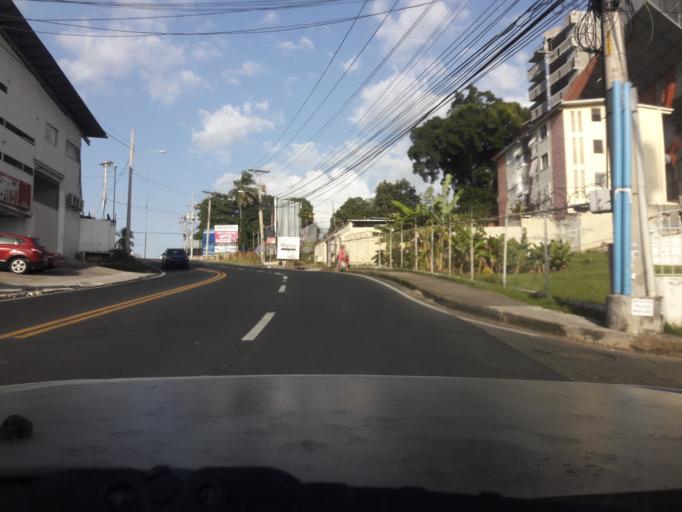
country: PA
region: Panama
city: Panama
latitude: 9.0141
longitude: -79.5076
